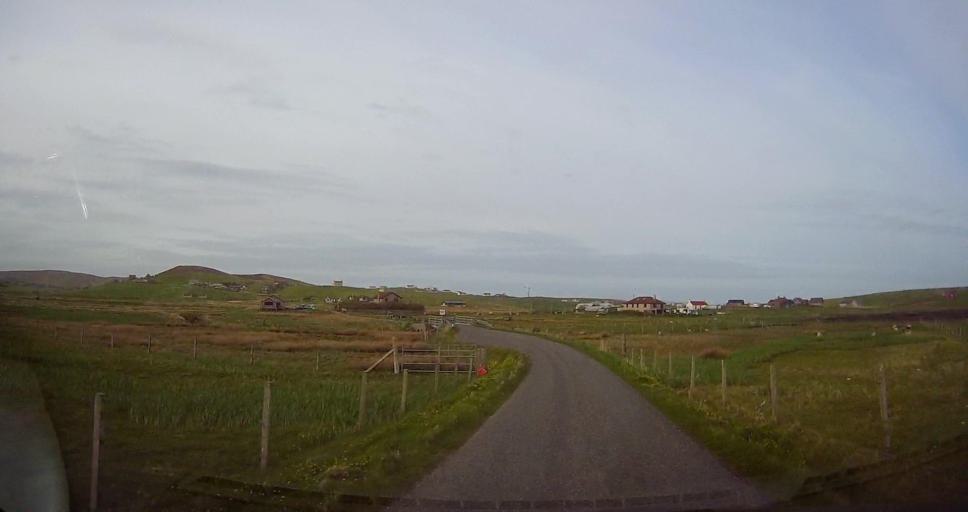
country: GB
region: Scotland
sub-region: Shetland Islands
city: Sandwick
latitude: 60.0419
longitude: -1.2173
